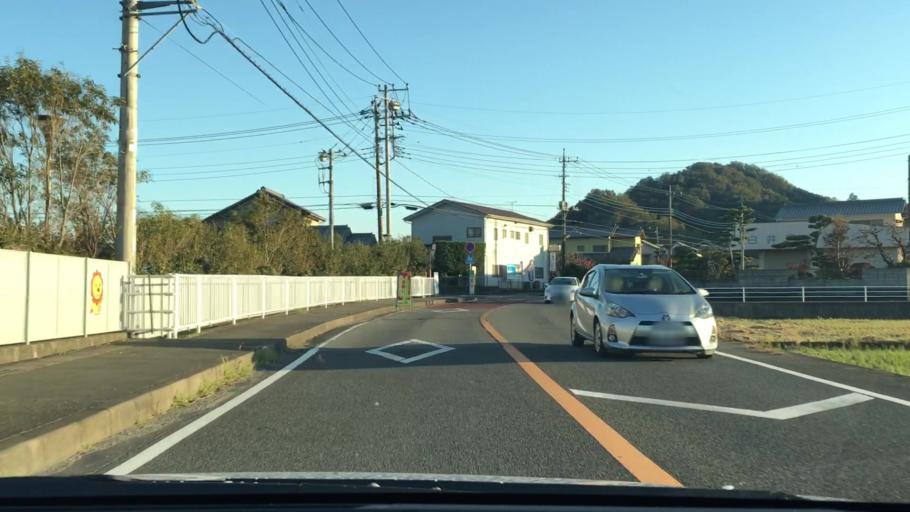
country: JP
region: Shizuoka
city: Mishima
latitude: 35.0729
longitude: 138.9307
